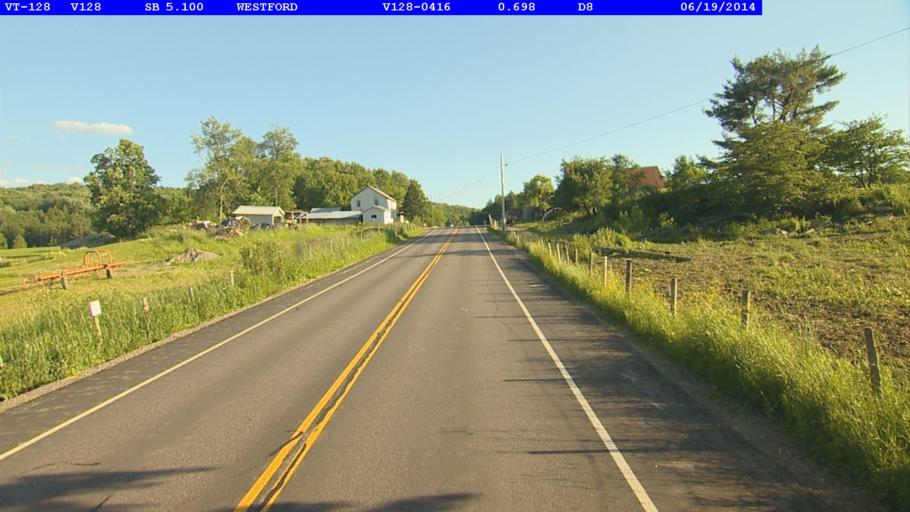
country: US
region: Vermont
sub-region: Chittenden County
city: Jericho
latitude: 44.5684
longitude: -73.0228
